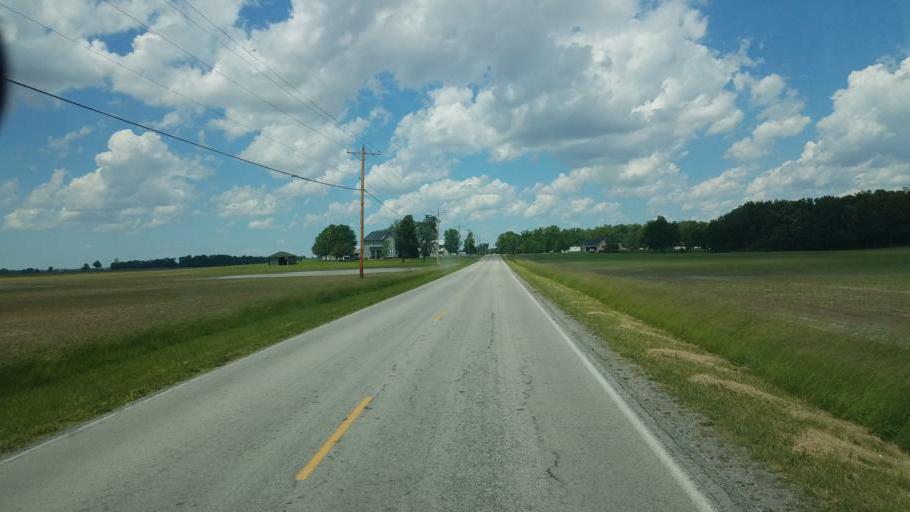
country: US
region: Ohio
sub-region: Wyandot County
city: Upper Sandusky
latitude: 40.7752
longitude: -83.2679
